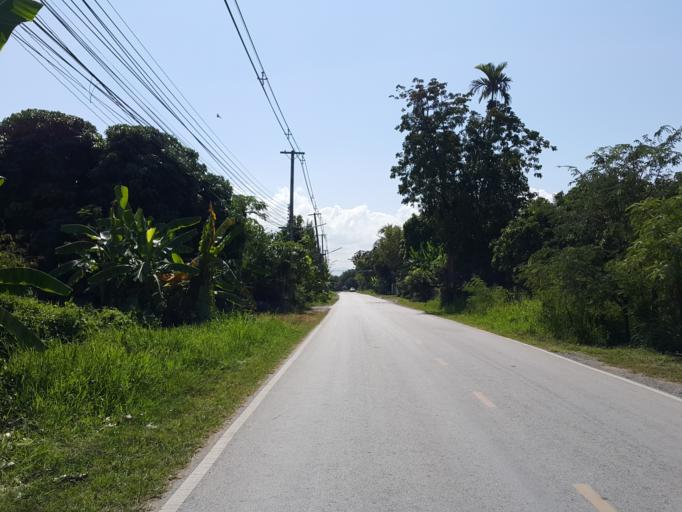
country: TH
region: Chiang Mai
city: San Kamphaeng
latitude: 18.8413
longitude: 99.1490
